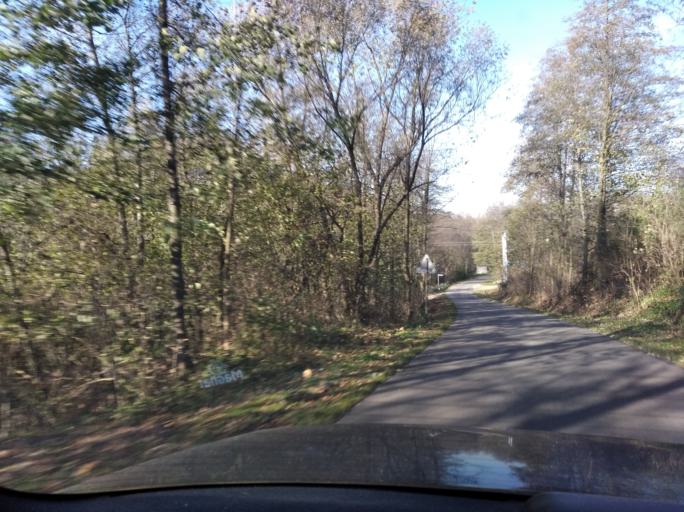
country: PL
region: Subcarpathian Voivodeship
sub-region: Powiat ropczycko-sedziszowski
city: Wielopole Skrzynskie
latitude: 49.9012
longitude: 21.5708
